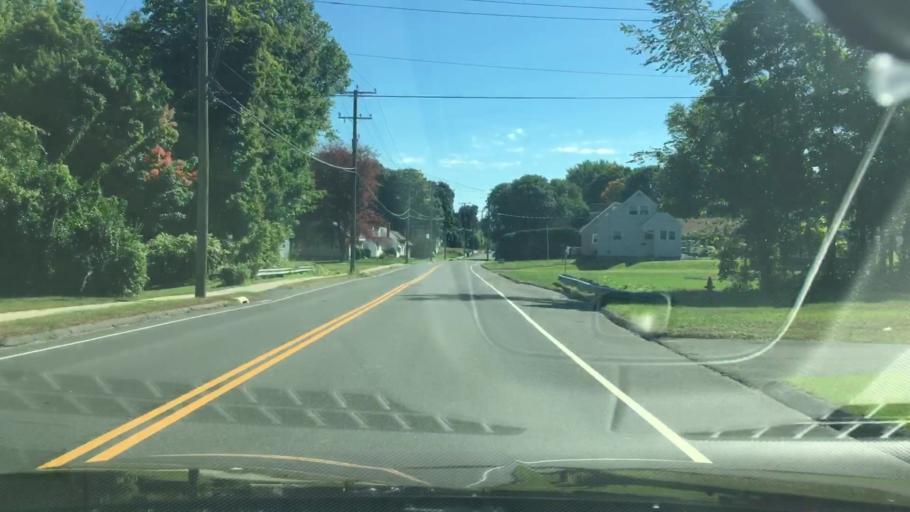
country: US
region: Connecticut
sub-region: Hartford County
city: Bristol
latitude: 41.6847
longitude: -72.9093
